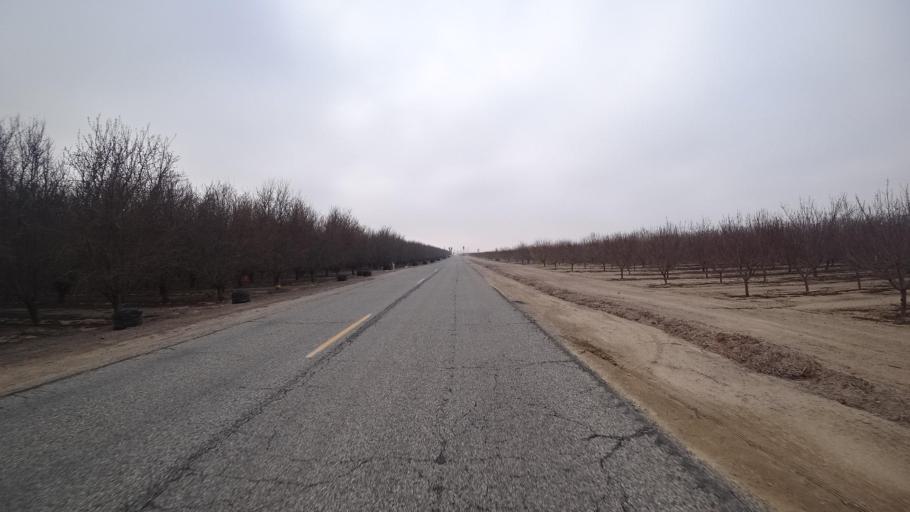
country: US
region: California
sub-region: Kern County
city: Maricopa
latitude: 35.1231
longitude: -119.3536
